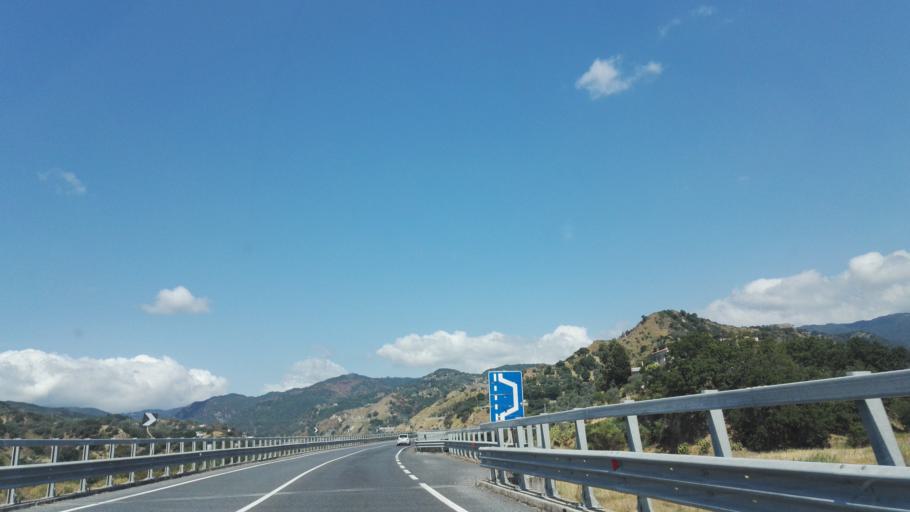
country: IT
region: Calabria
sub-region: Provincia di Reggio Calabria
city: Grotteria
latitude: 38.3448
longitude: 16.2596
